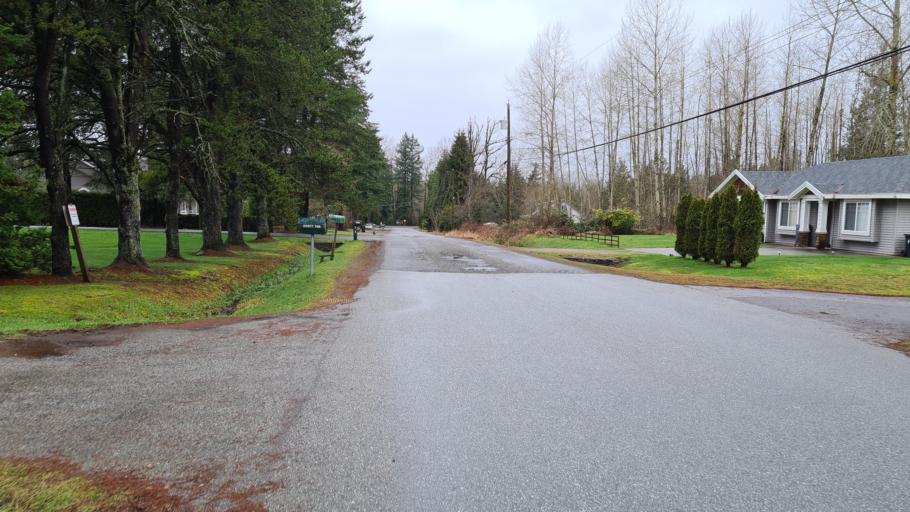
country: CA
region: British Columbia
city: Walnut Grove
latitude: 49.1384
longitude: -122.6579
